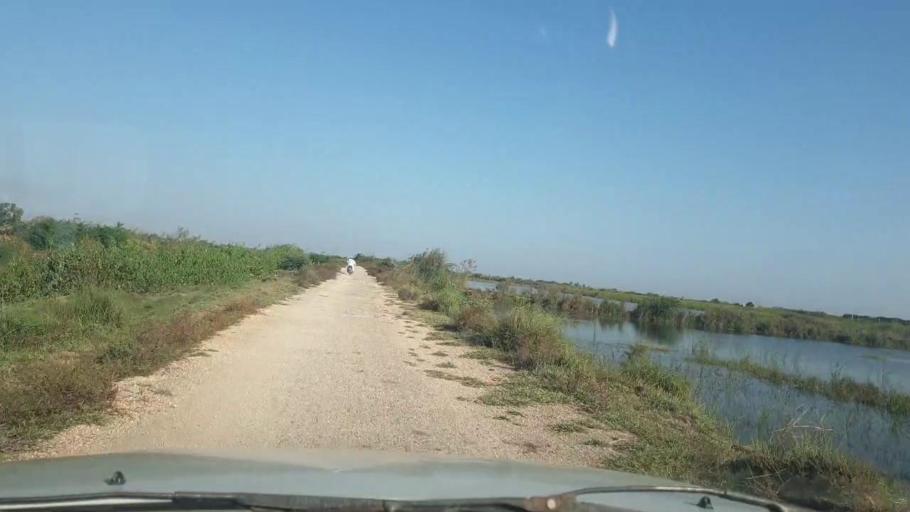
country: PK
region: Sindh
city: Chuhar Jamali
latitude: 24.5489
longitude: 67.9102
